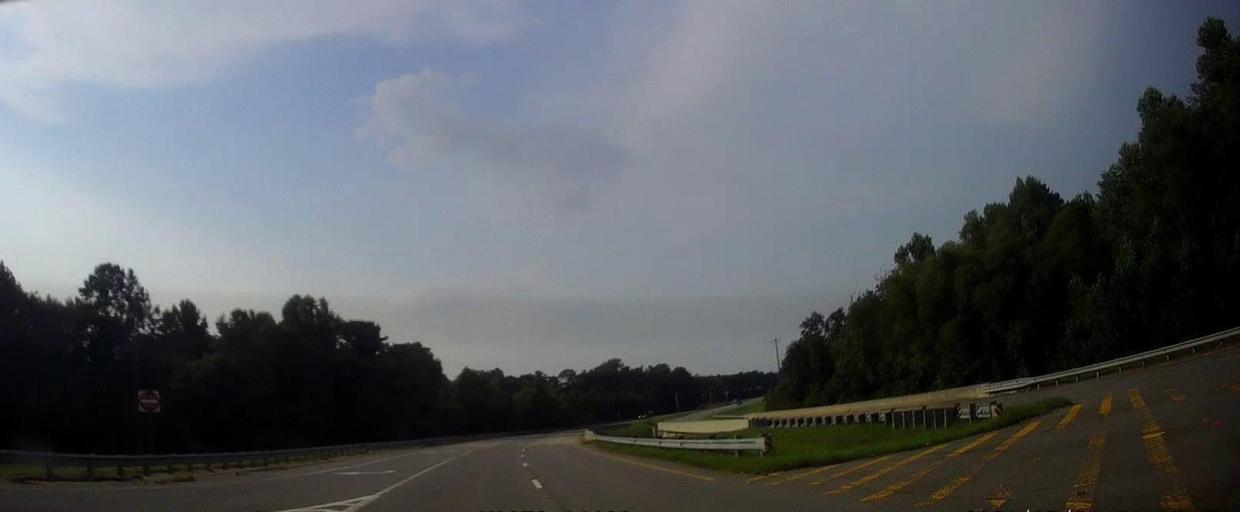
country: US
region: Georgia
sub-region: Laurens County
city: Dublin
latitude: 32.5458
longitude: -82.9782
